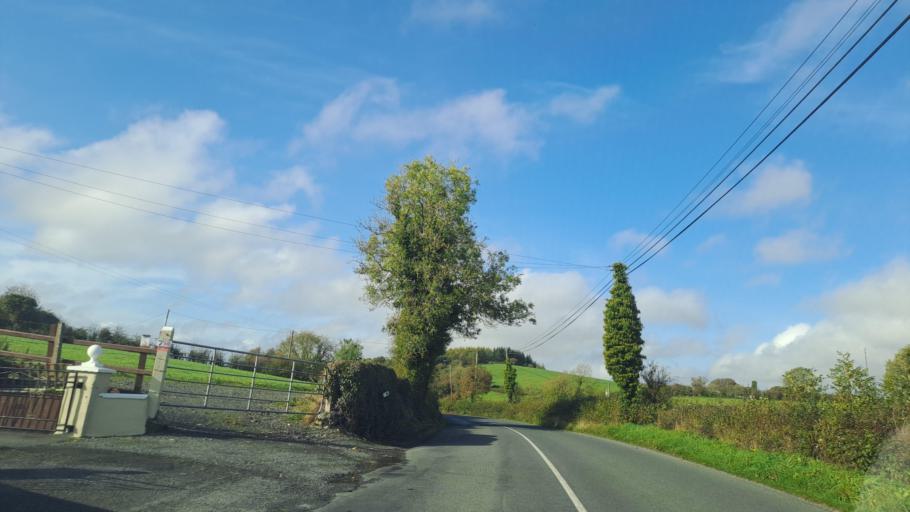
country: IE
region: Ulster
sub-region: An Cabhan
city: Bailieborough
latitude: 54.0233
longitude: -6.9402
